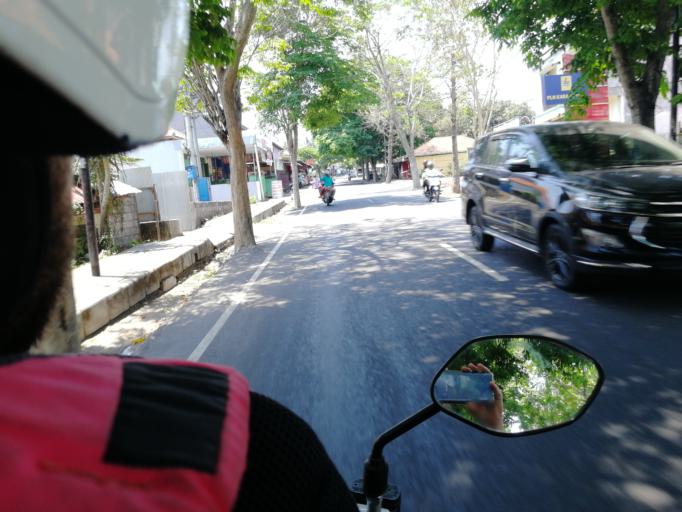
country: ID
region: Bali
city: Subagan
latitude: -8.4559
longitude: 115.5973
